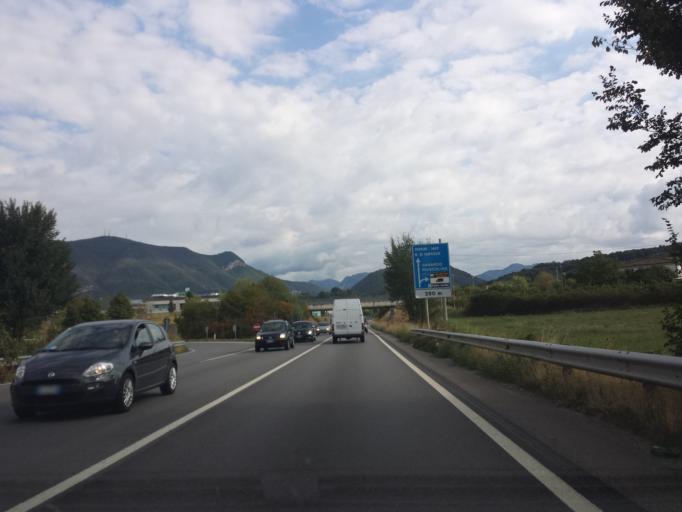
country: IT
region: Lombardy
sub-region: Provincia di Brescia
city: Gavardo-Sopraponte
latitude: 45.5742
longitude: 10.4428
